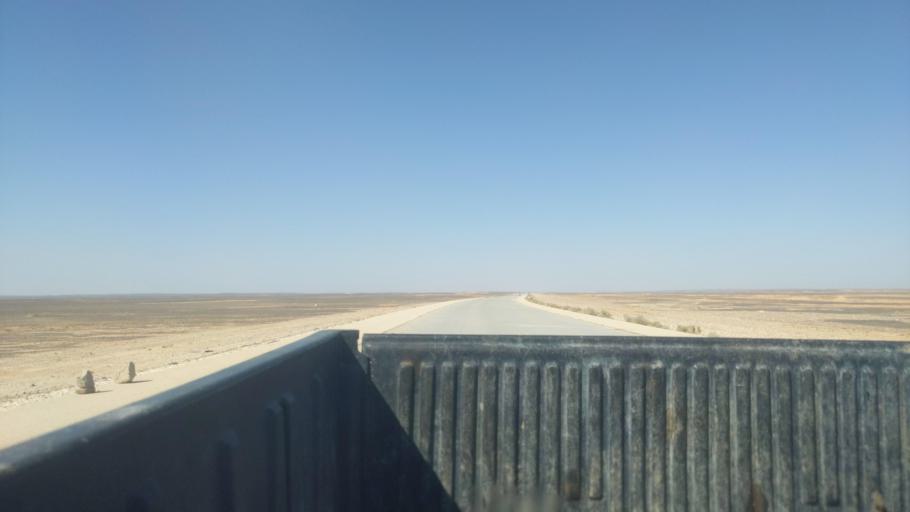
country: JO
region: Amman
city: Al Azraq ash Shamali
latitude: 31.4619
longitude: 36.7975
